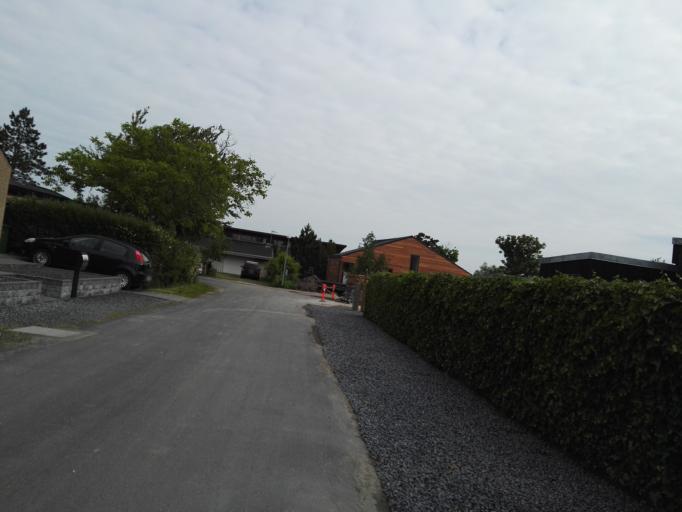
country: DK
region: Zealand
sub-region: Roskilde Kommune
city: Jyllinge
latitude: 55.7766
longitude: 12.0897
